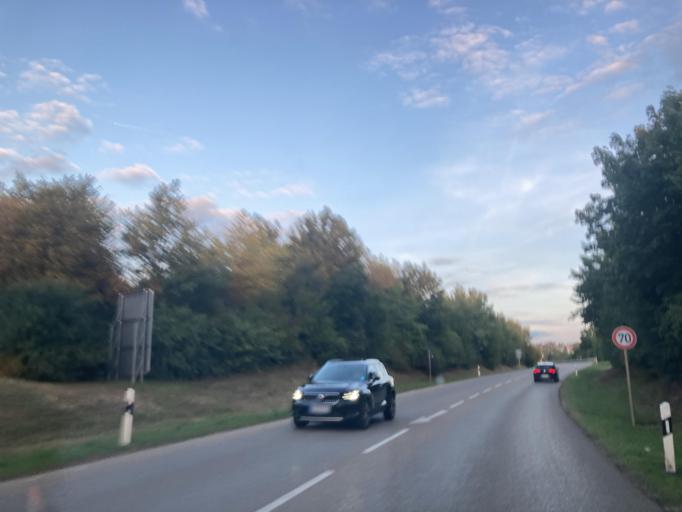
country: DE
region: Bavaria
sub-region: Swabia
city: Noerdlingen
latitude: 48.8546
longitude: 10.4783
